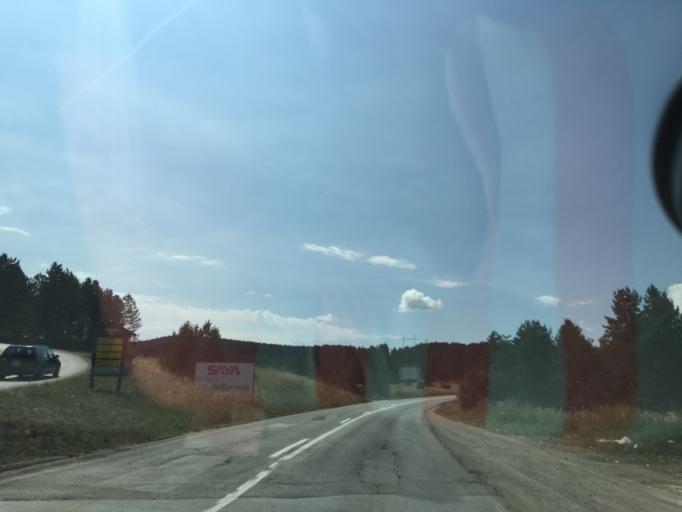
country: RS
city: Zlatibor
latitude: 43.7223
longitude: 19.7063
